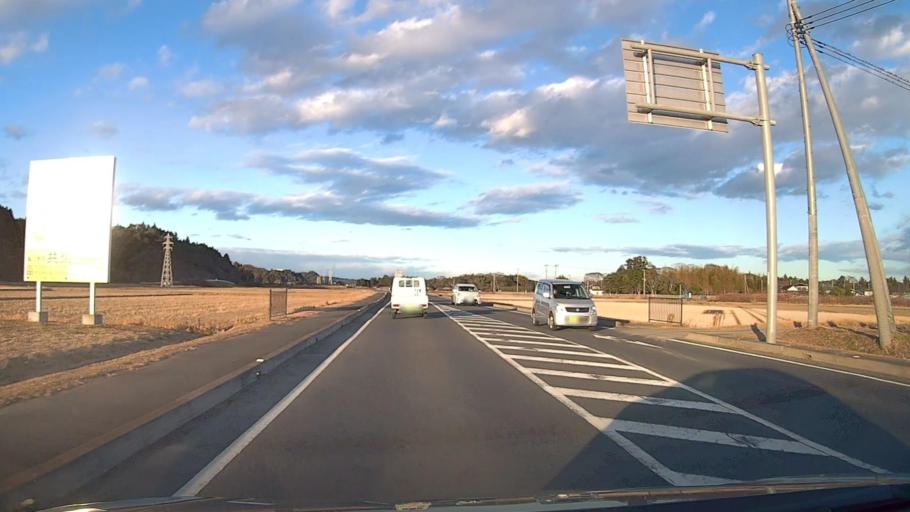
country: JP
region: Ibaraki
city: Kitaibaraki
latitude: 36.8229
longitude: 140.7648
